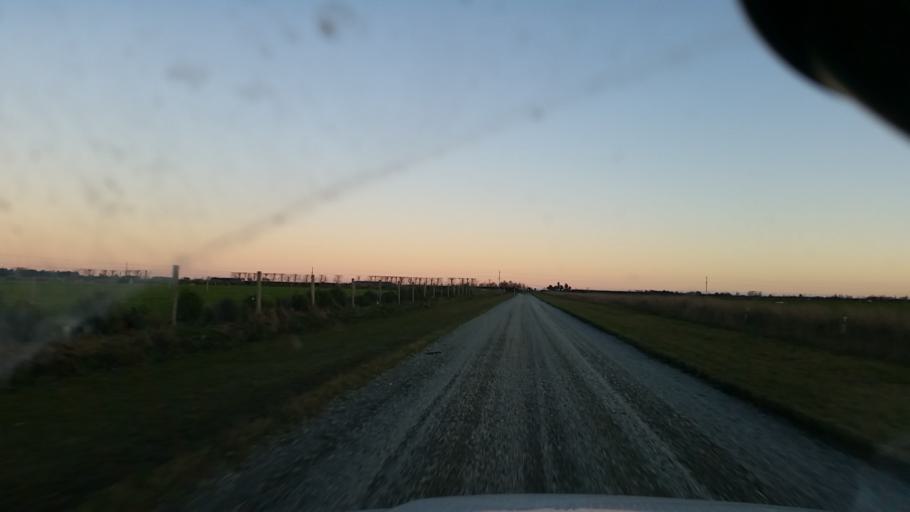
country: NZ
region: Canterbury
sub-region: Ashburton District
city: Tinwald
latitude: -44.0643
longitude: 171.6605
